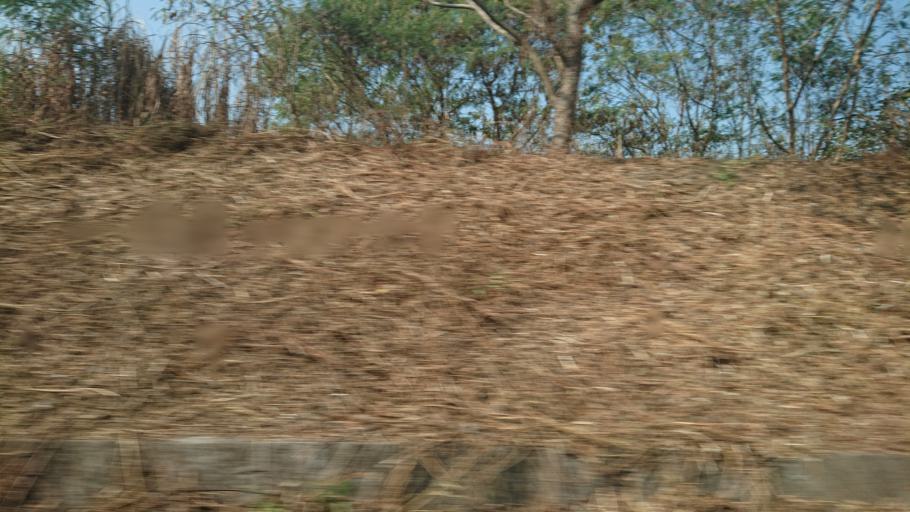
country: TW
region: Taiwan
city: Lugu
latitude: 23.7428
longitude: 120.6584
